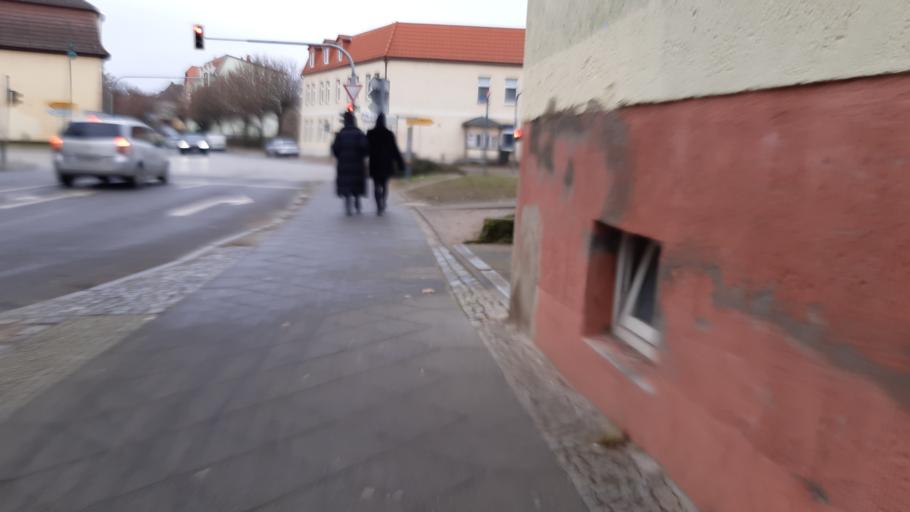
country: DE
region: Brandenburg
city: Templin
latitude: 53.1181
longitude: 13.5091
